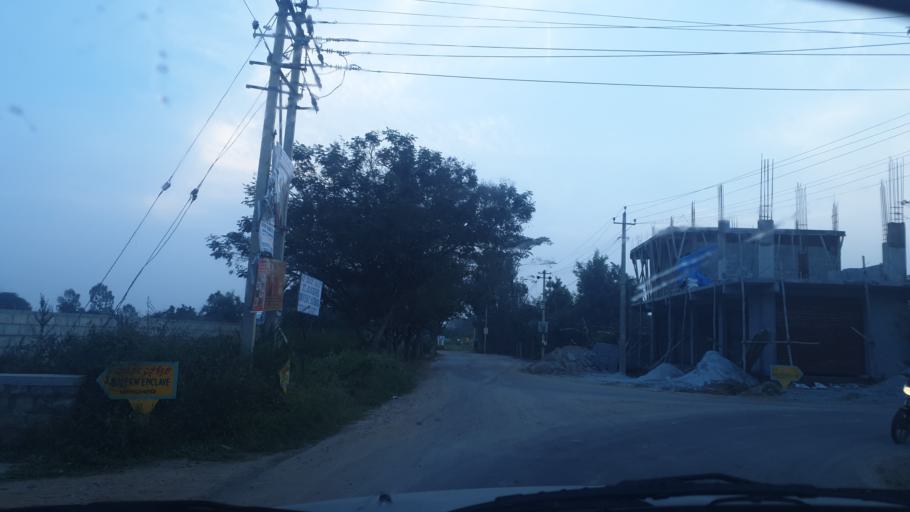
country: IN
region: Karnataka
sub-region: Bangalore Rural
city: Hoskote
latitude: 13.0765
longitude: 77.7042
